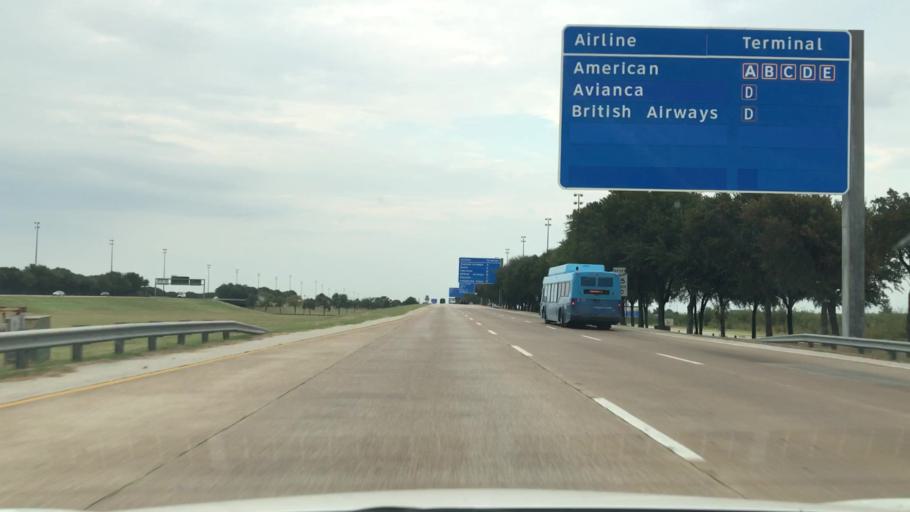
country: US
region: Texas
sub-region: Tarrant County
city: Euless
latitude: 32.8696
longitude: -97.0400
